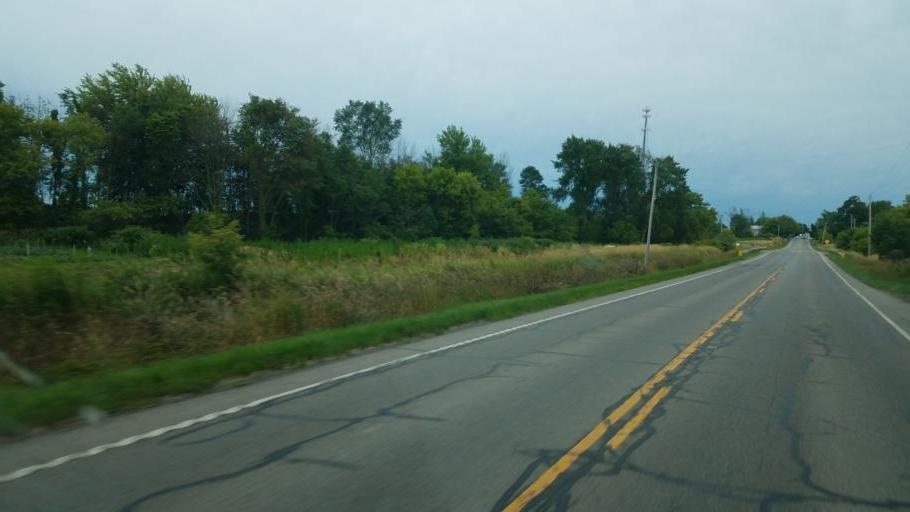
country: US
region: Ohio
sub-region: Huron County
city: Greenwich
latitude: 40.9186
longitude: -82.4985
